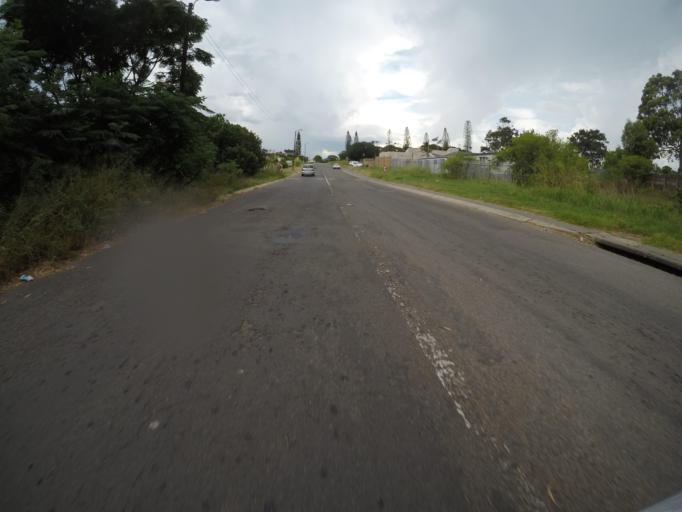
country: ZA
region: Eastern Cape
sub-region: Buffalo City Metropolitan Municipality
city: East London
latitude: -33.0246
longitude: 27.8602
